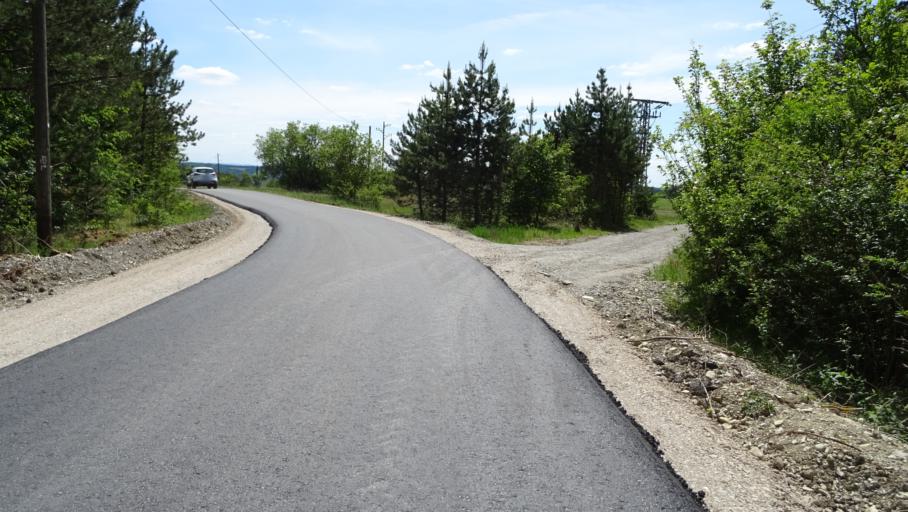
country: DE
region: Baden-Wuerttemberg
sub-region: Karlsruhe Region
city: Seckach
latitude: 49.4794
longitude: 9.3267
